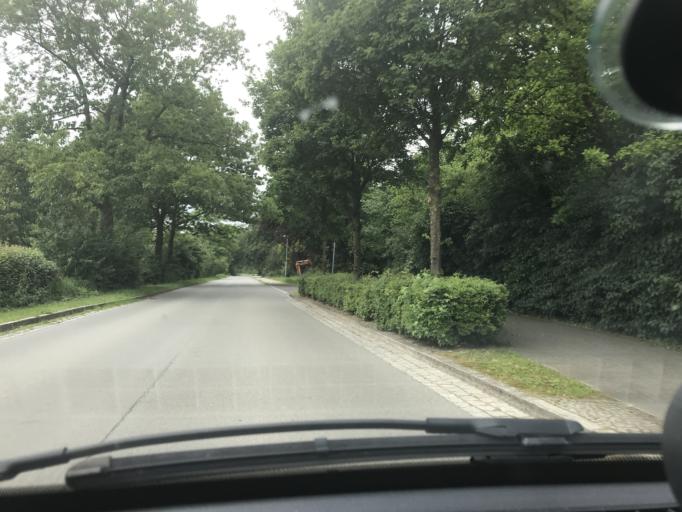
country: DE
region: Schleswig-Holstein
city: Rausdorf
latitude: 53.5917
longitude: 10.3326
